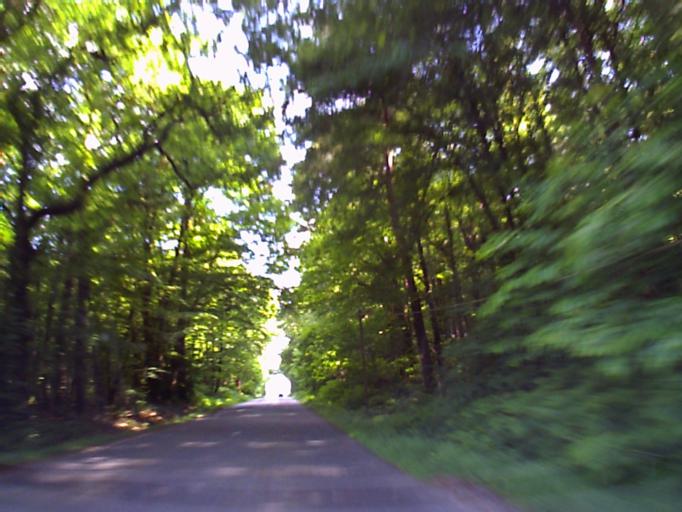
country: FR
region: Brittany
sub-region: Departement d'Ille-et-Vilaine
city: Iffendic
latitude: 48.1568
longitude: -2.0137
